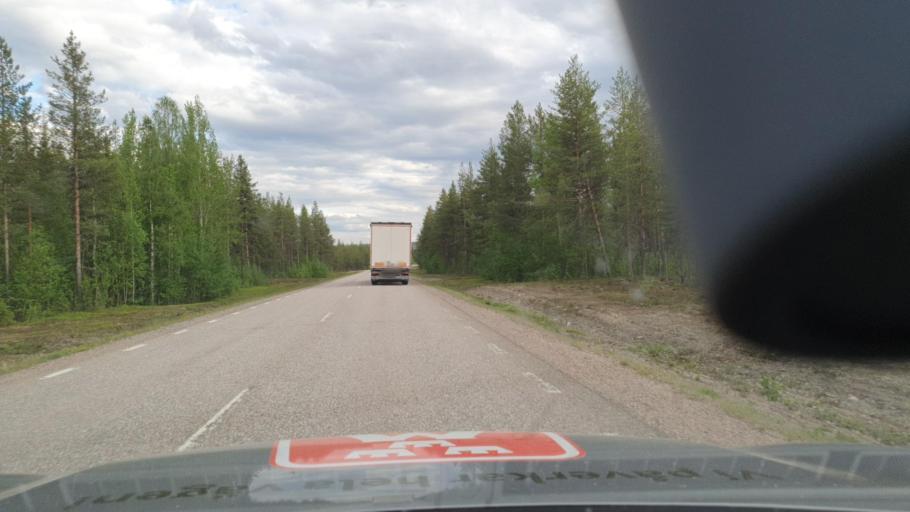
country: SE
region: Norrbotten
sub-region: Gallivare Kommun
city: Gaellivare
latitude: 67.1212
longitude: 20.9032
